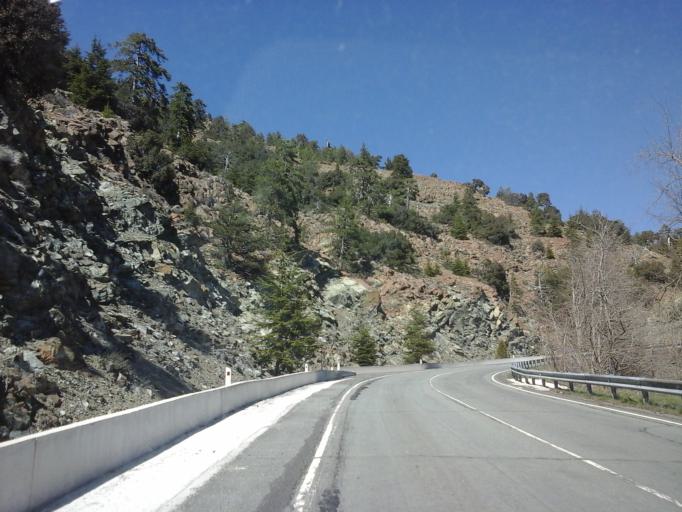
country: CY
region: Lefkosia
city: Kakopetria
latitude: 34.9201
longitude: 32.8737
